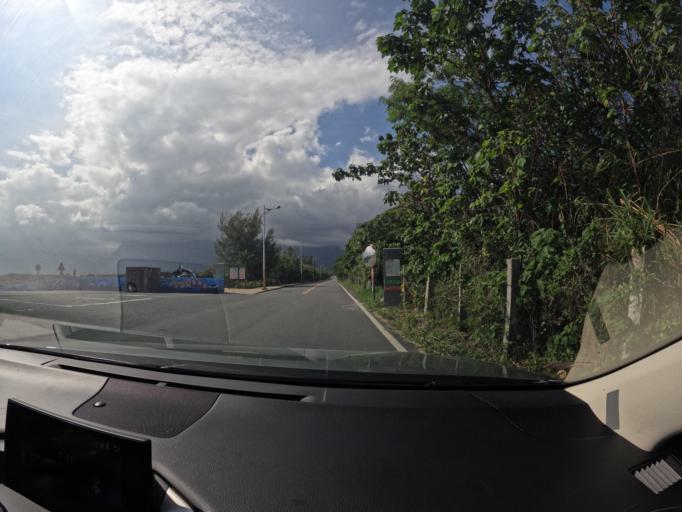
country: TW
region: Taiwan
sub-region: Hualien
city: Hualian
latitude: 24.0192
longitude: 121.6357
